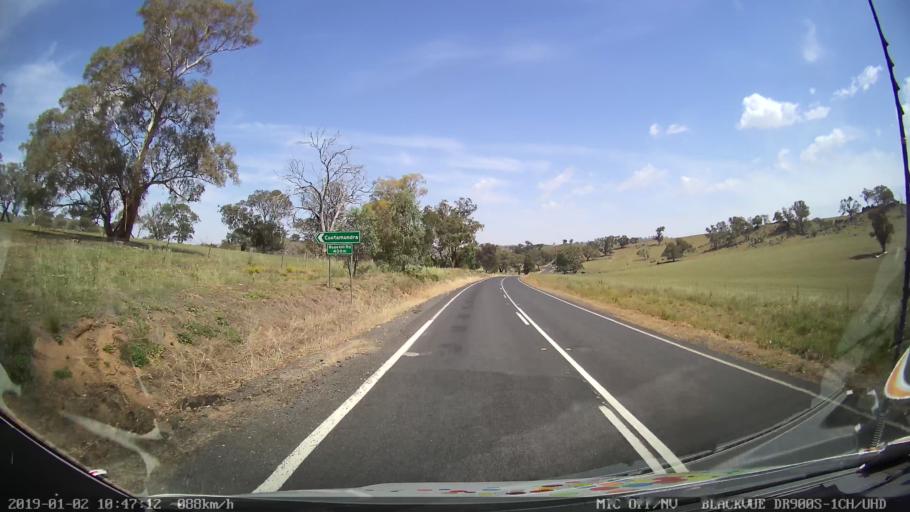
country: AU
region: New South Wales
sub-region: Cootamundra
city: Cootamundra
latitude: -34.7474
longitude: 148.2759
